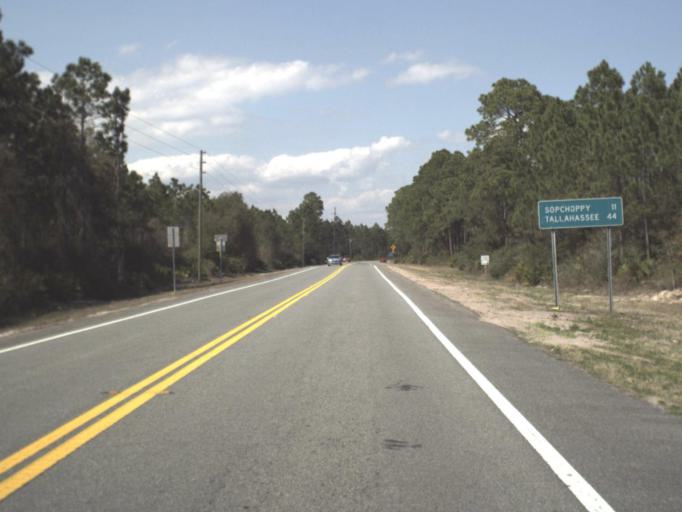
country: US
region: Florida
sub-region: Franklin County
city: Carrabelle
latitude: 29.9204
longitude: -84.5203
